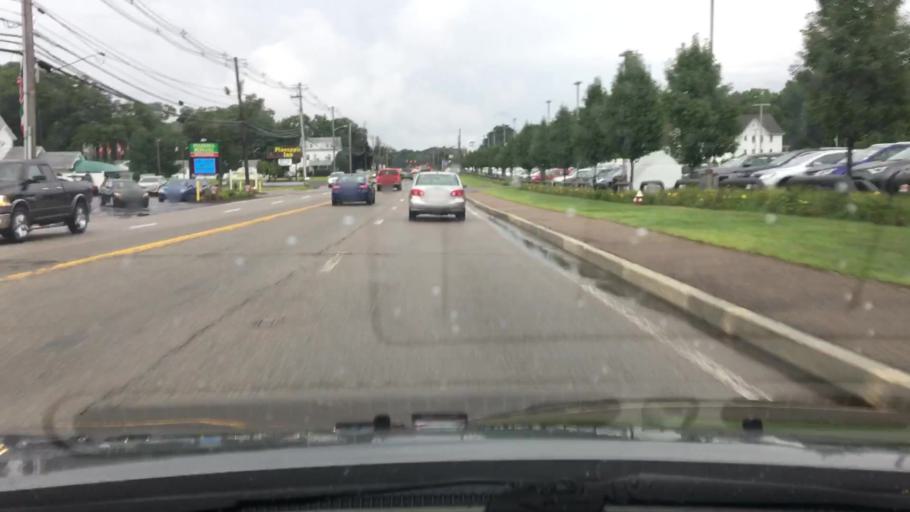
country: US
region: Massachusetts
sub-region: Norfolk County
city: Plainville
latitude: 41.9604
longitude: -71.3413
